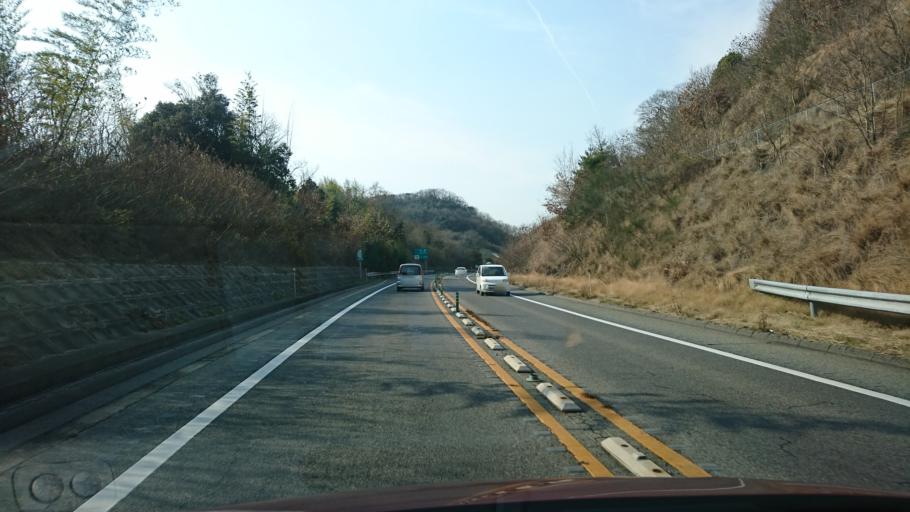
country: JP
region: Hiroshima
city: Onomichi
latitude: 34.3879
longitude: 133.2040
